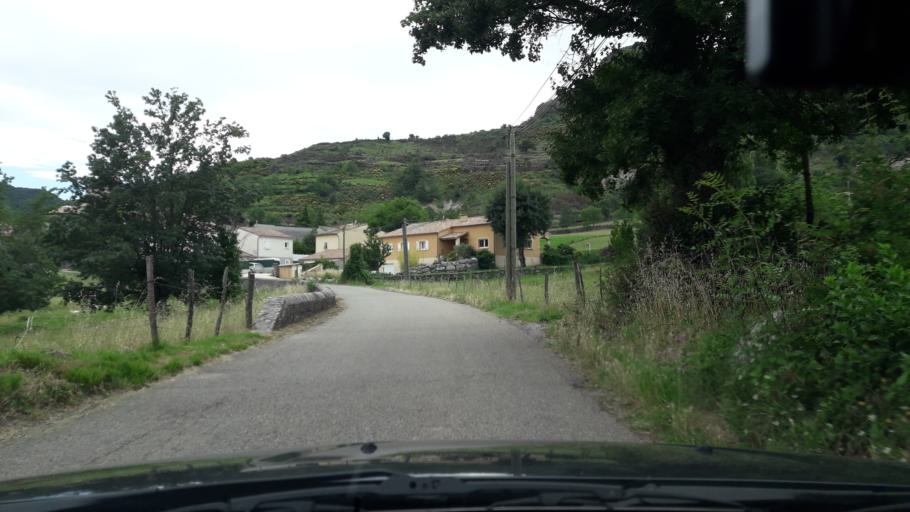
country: FR
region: Rhone-Alpes
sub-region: Departement de l'Ardeche
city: Alissas
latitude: 44.6808
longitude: 4.6275
